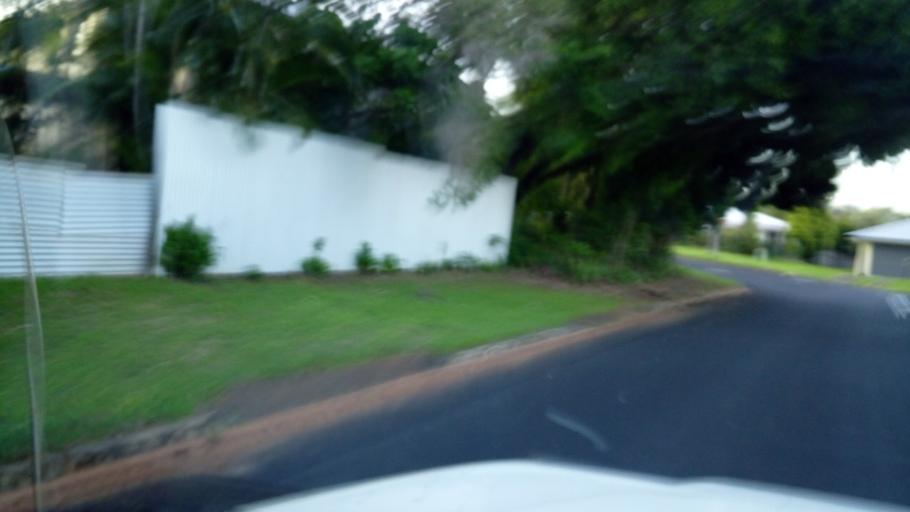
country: AU
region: Queensland
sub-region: Cairns
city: Woree
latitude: -16.9560
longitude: 145.7333
